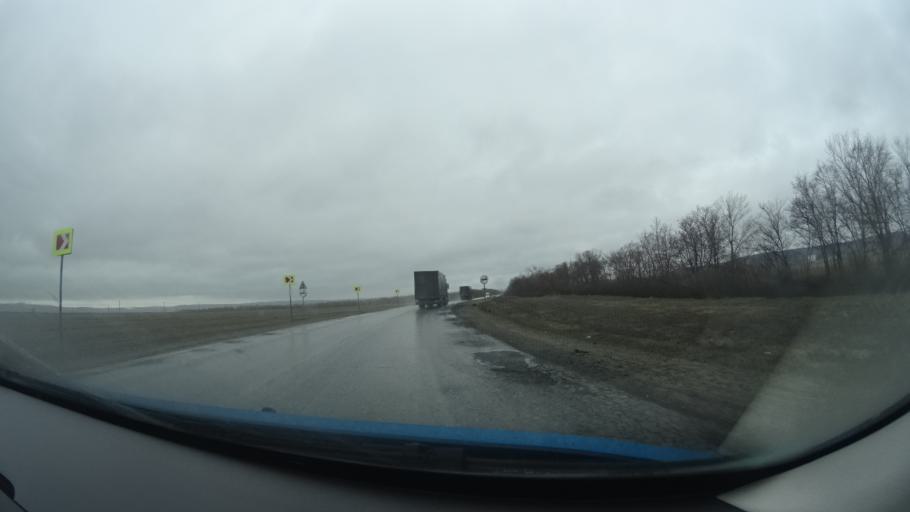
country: RU
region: Bashkortostan
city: Kandry
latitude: 54.5351
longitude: 54.1163
